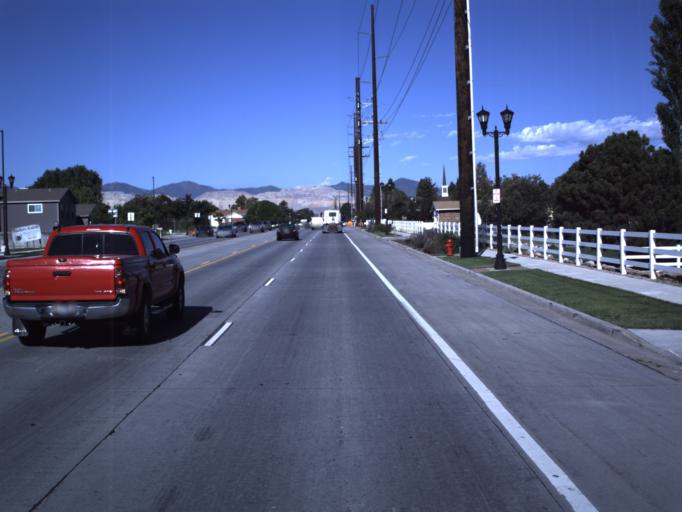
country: US
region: Utah
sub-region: Salt Lake County
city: South Jordan
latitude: 40.5442
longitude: -111.9318
